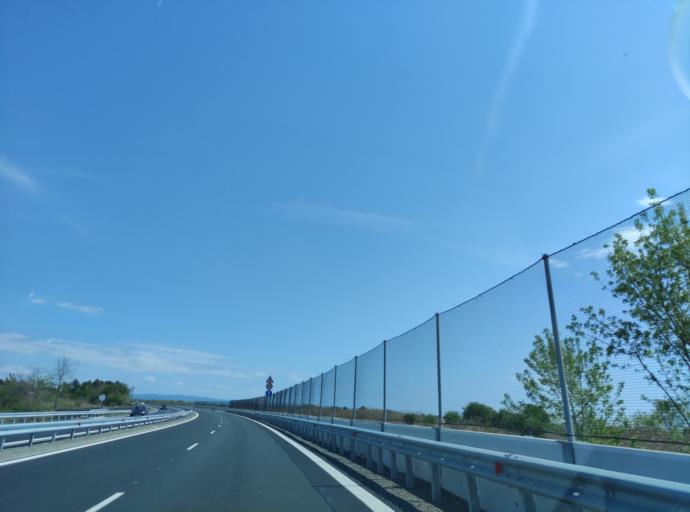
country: BG
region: Burgas
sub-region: Obshtina Pomorie
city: Pomorie
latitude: 42.5933
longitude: 27.6129
